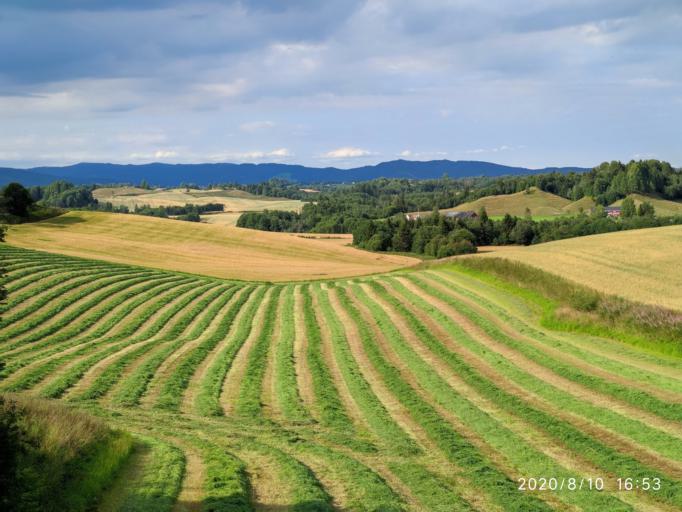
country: NO
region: Akershus
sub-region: Nannestad
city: Teigebyen
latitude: 60.1705
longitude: 11.0200
